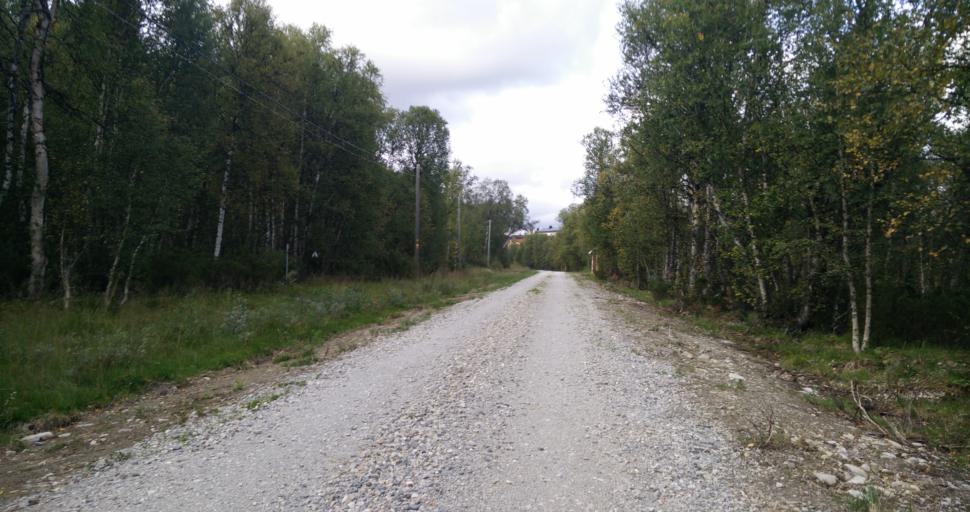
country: NO
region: Sor-Trondelag
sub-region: Tydal
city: Aas
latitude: 62.6360
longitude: 12.4185
